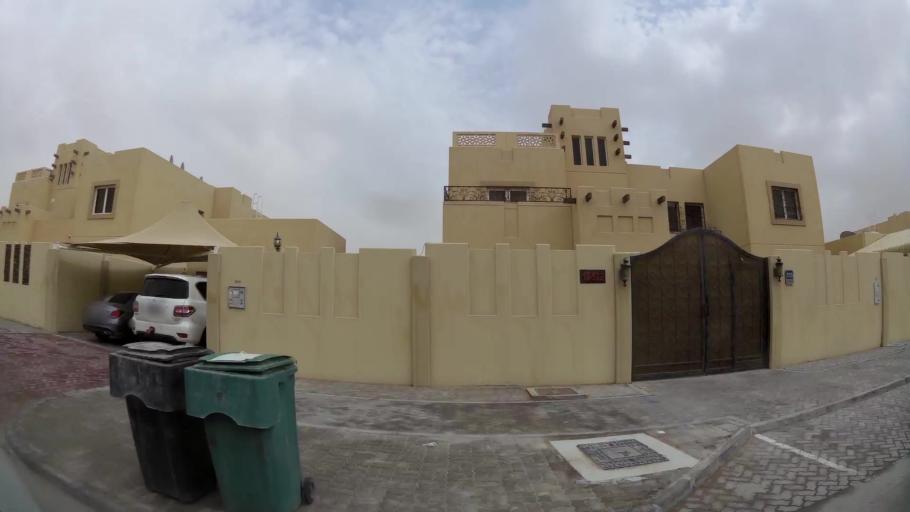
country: AE
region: Abu Dhabi
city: Abu Dhabi
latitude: 24.4521
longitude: 54.7154
